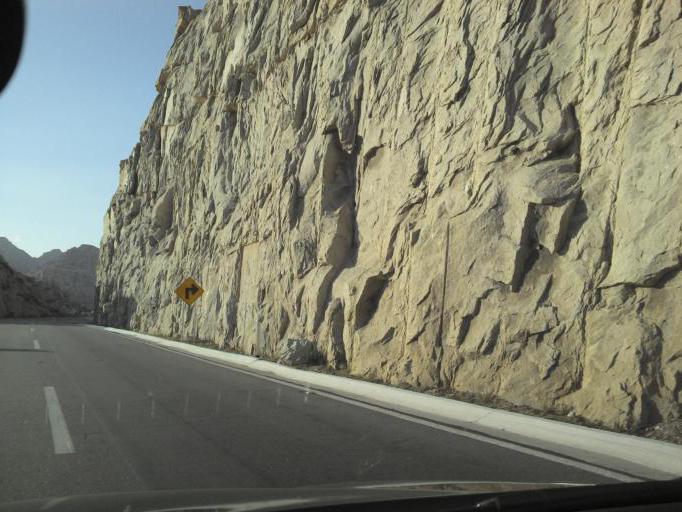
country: MX
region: Baja California
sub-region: Tecate
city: Cereso del Hongo
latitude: 32.5744
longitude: -116.0402
